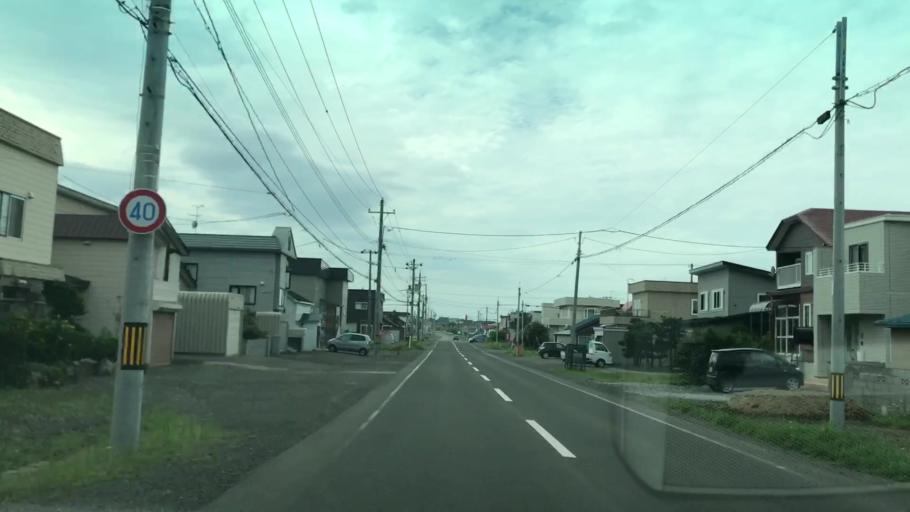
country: JP
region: Hokkaido
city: Iwanai
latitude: 42.9770
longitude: 140.5073
